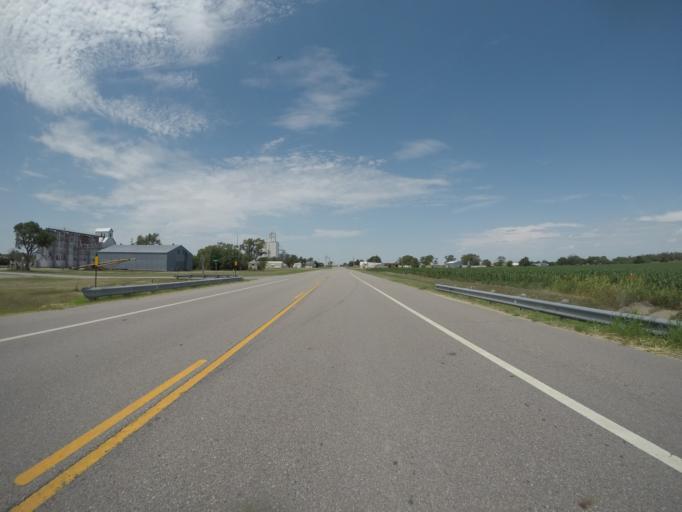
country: US
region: Kansas
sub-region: Rooks County
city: Stockton
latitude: 39.4561
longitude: -99.0969
